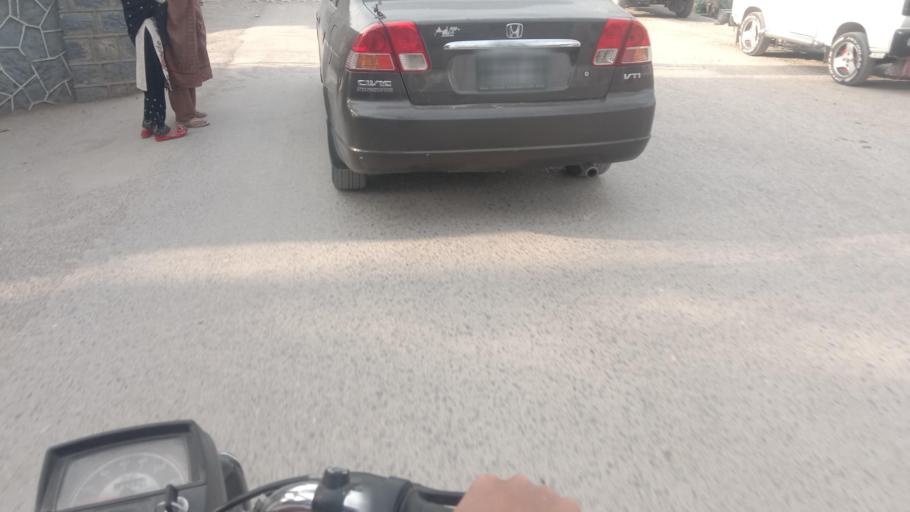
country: PK
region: Khyber Pakhtunkhwa
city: Abbottabad
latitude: 34.1606
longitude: 73.2636
